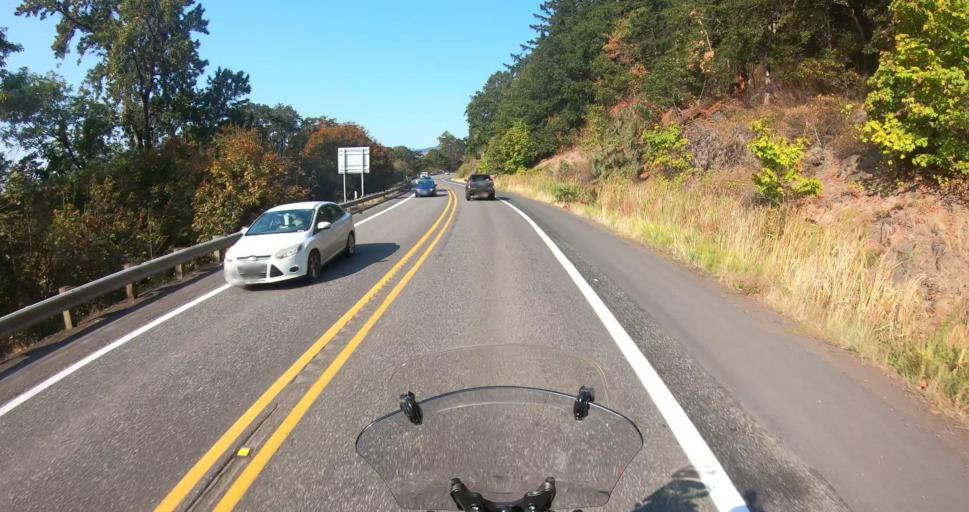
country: US
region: Washington
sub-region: Klickitat County
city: White Salmon
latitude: 45.7255
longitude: -121.4969
